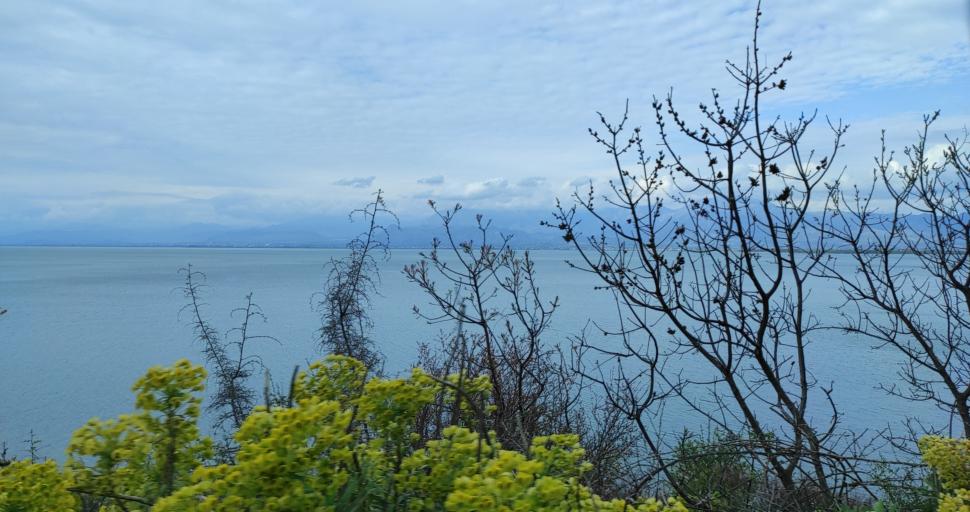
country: AL
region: Shkoder
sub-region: Rrethi i Shkodres
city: Dajc
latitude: 42.0680
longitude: 19.4221
